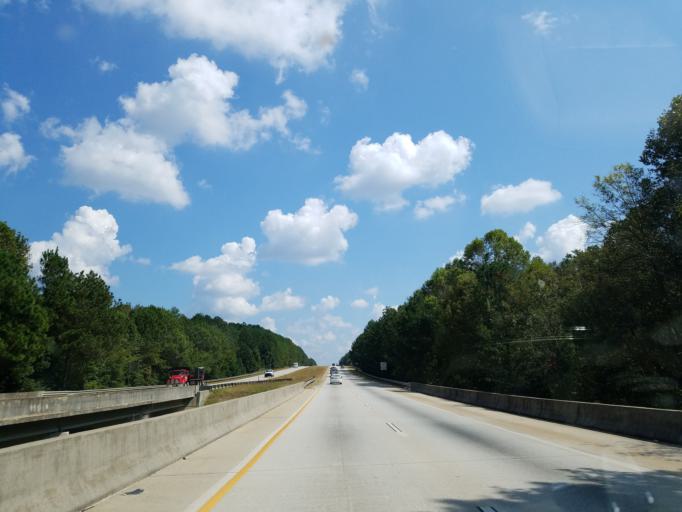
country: US
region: Georgia
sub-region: Barrow County
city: Auburn
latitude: 33.9700
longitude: -83.8337
